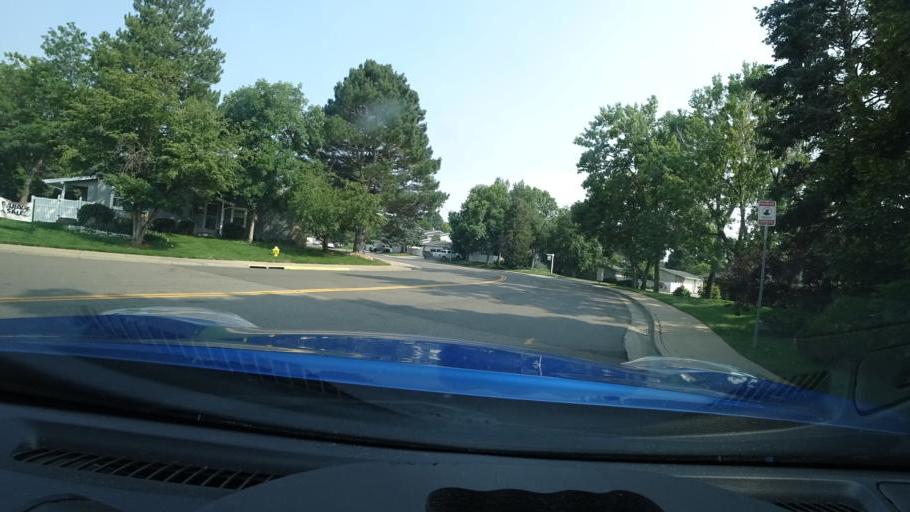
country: US
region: Colorado
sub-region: Adams County
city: Aurora
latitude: 39.6675
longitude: -104.8334
